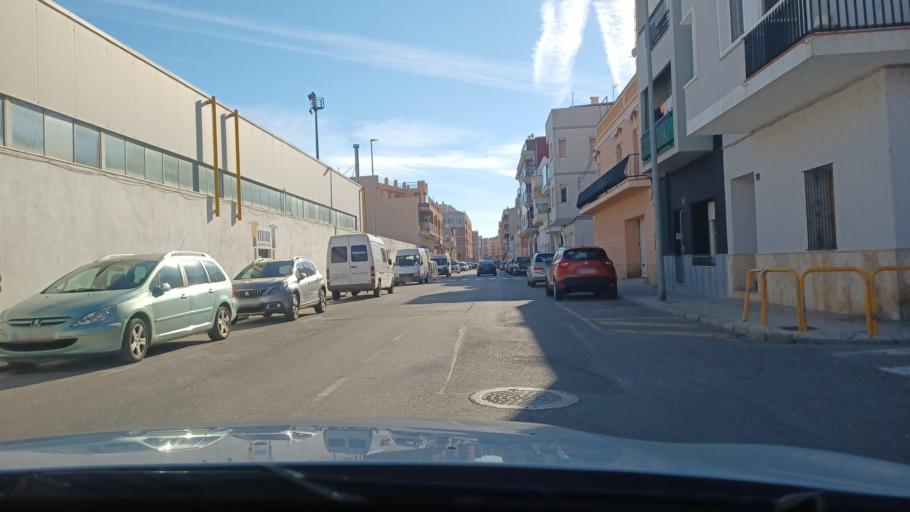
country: ES
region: Catalonia
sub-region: Provincia de Tarragona
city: Amposta
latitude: 40.7077
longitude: 0.5807
